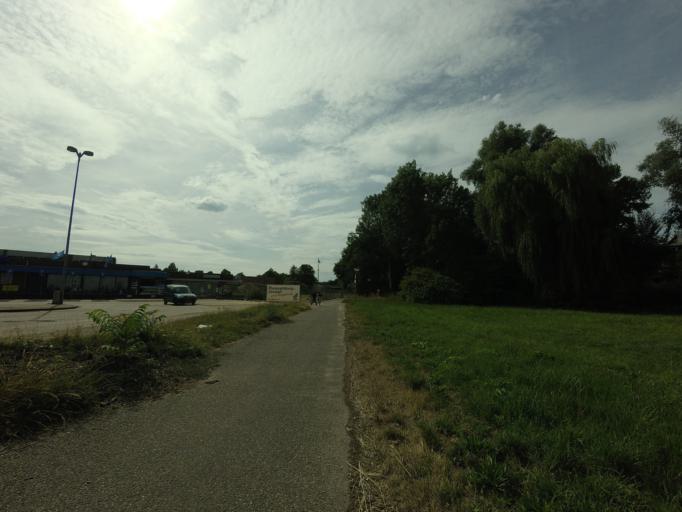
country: NL
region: Utrecht
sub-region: Gemeente Zeist
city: Zeist
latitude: 52.0839
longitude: 5.2202
